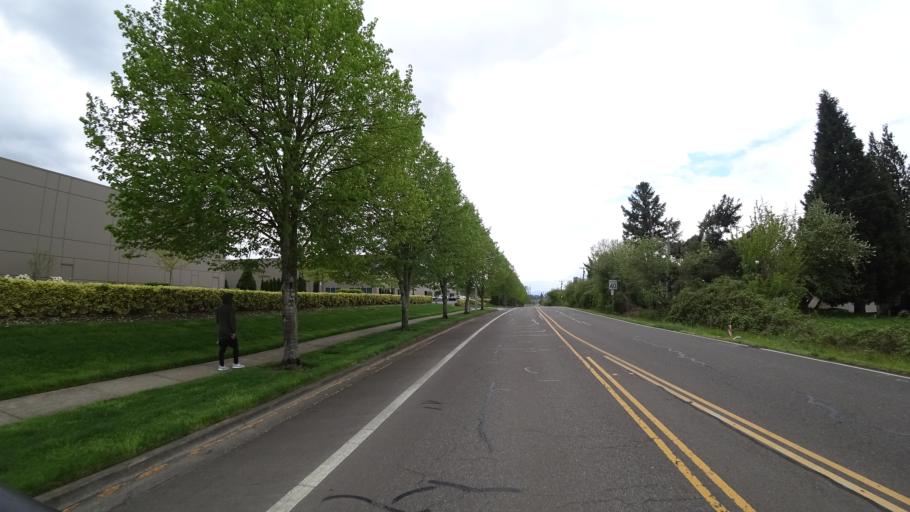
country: US
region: Oregon
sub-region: Washington County
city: Rockcreek
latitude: 45.5654
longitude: -122.9189
